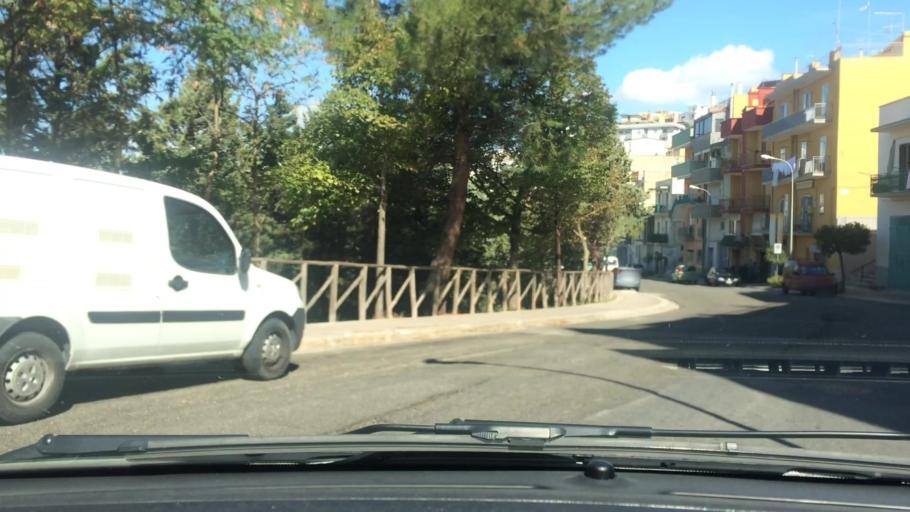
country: IT
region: Basilicate
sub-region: Provincia di Matera
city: Montescaglioso
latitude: 40.5496
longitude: 16.6656
